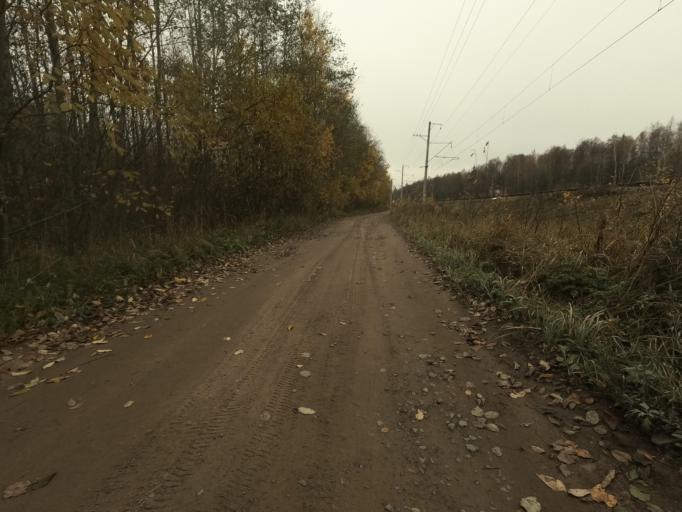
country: RU
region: Leningrad
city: Pavlovo
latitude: 59.7857
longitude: 30.8915
